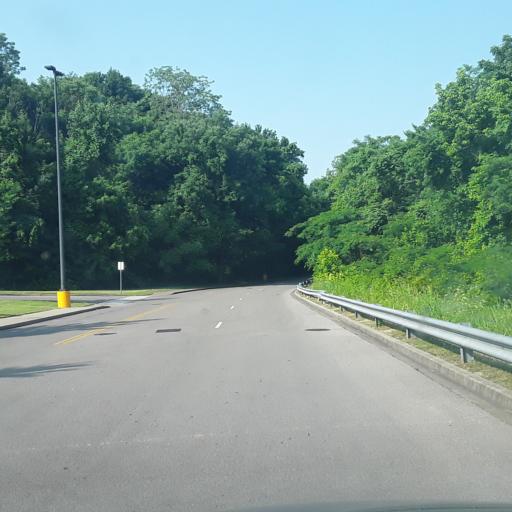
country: US
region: Tennessee
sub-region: Williamson County
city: Brentwood Estates
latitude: 36.0410
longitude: -86.7112
